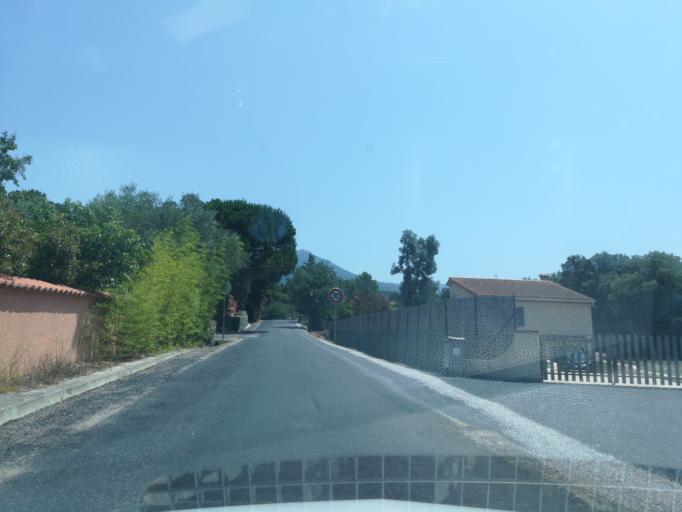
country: FR
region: Languedoc-Roussillon
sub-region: Departement des Pyrenees-Orientales
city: Maureillas-las-Illas
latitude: 42.4909
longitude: 2.8268
